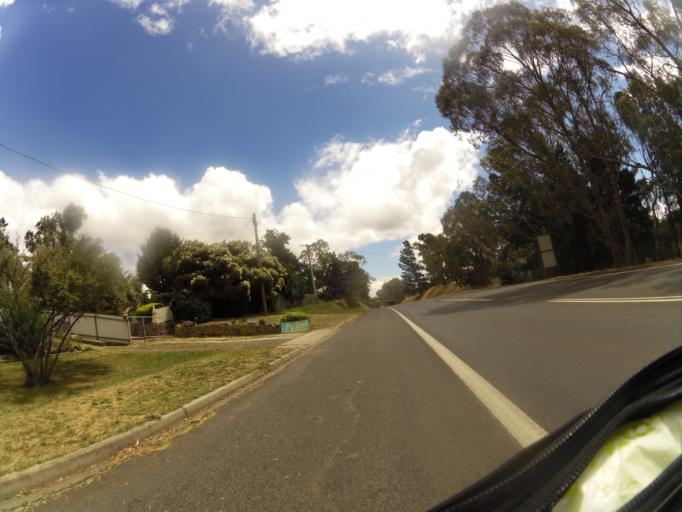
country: AU
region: Victoria
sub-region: Mount Alexander
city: Castlemaine
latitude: -37.0003
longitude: 144.2568
